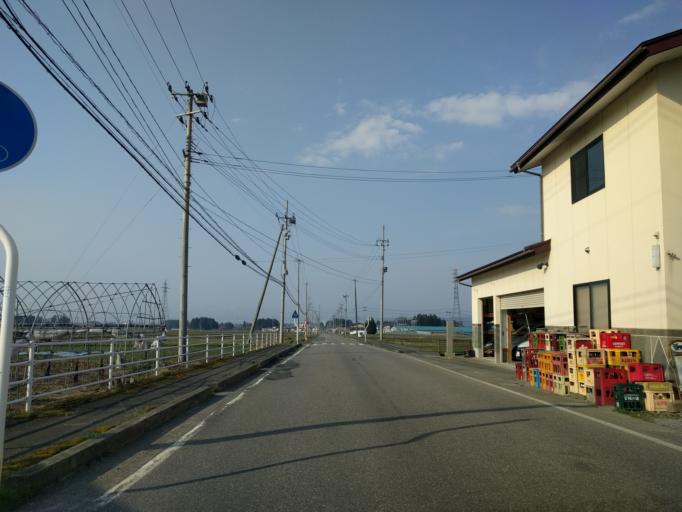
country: JP
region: Fukushima
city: Kitakata
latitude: 37.6769
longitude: 139.8949
